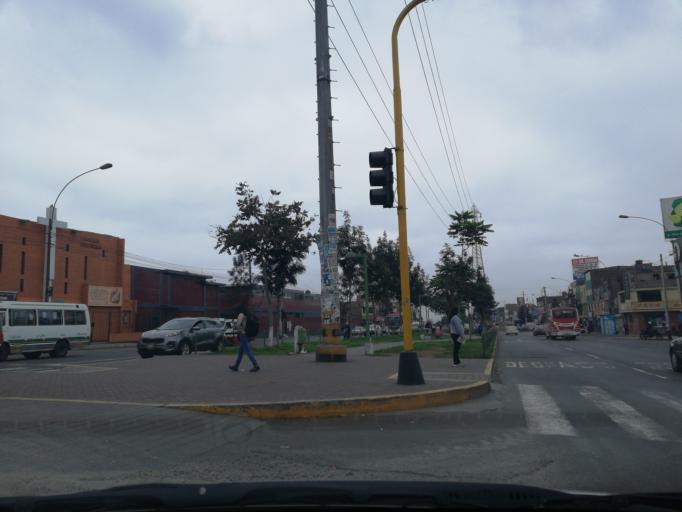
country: PE
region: Lima
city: Lima
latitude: -12.0320
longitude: -77.0662
